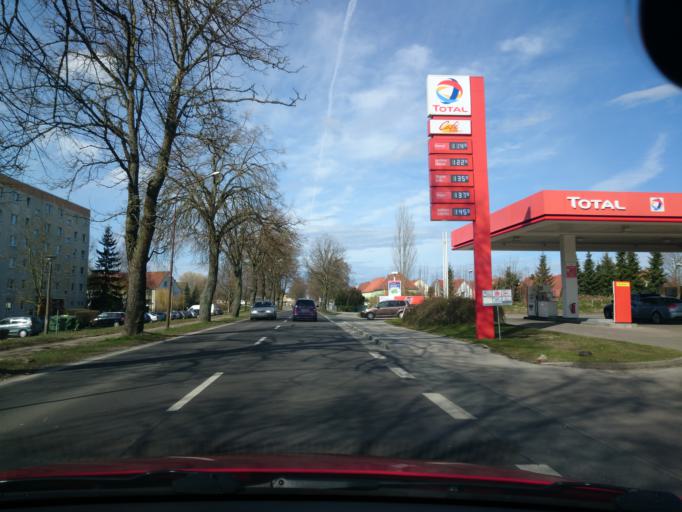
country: DE
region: Mecklenburg-Vorpommern
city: Barth
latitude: 54.3533
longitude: 12.7241
